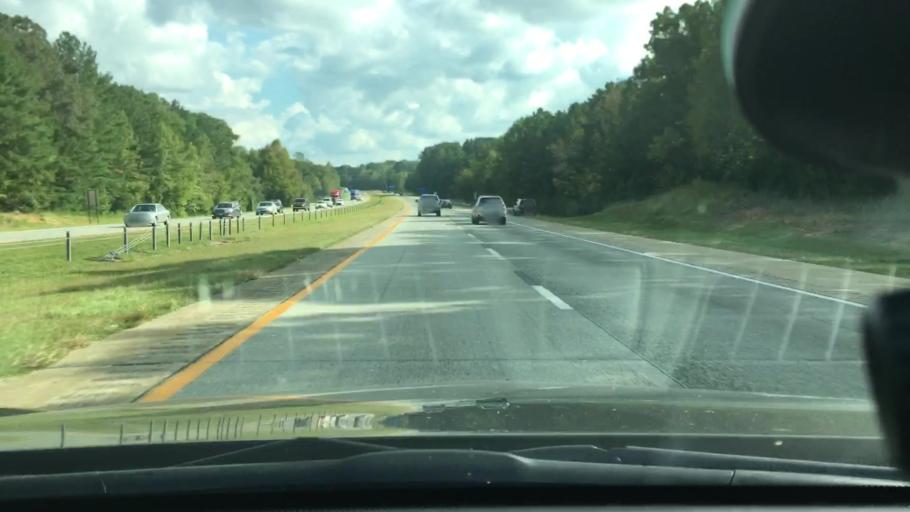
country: US
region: North Carolina
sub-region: Orange County
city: Chapel Hill
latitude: 35.9822
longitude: -79.0730
